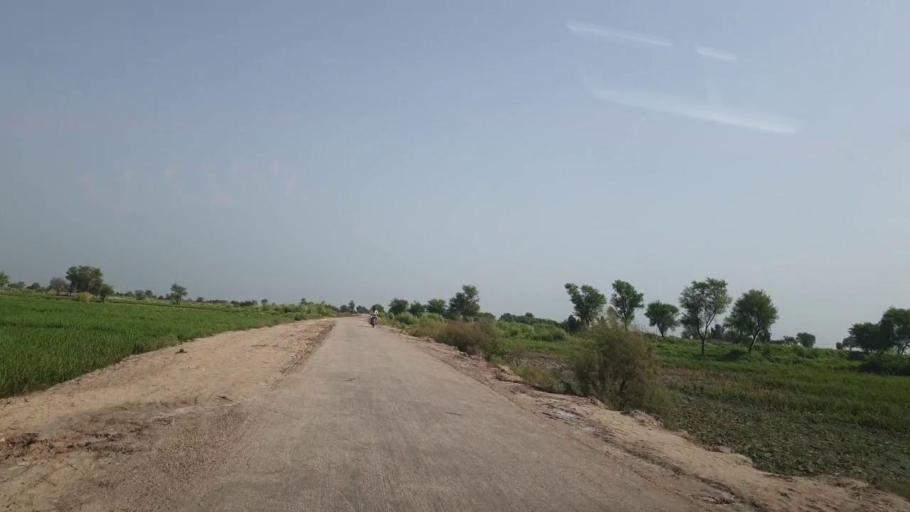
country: PK
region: Sindh
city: Sakrand
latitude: 26.2860
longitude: 68.2265
